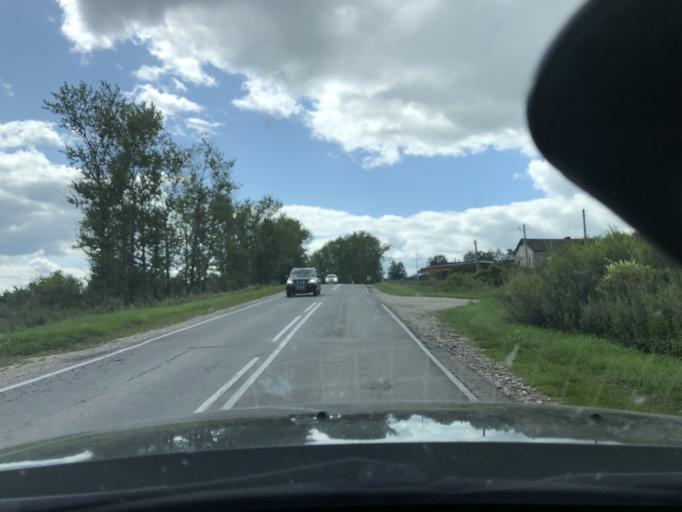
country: RU
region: Tula
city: Revyakino
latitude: 54.3599
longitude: 37.6385
